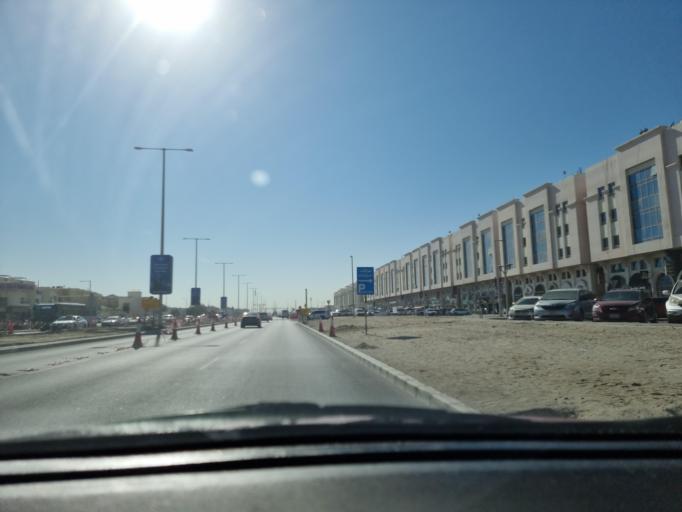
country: AE
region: Abu Dhabi
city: Abu Dhabi
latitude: 24.4234
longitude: 54.5653
